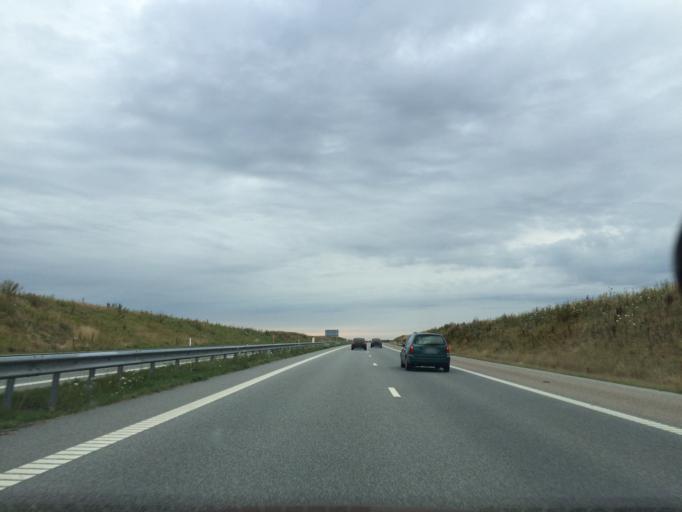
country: DK
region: South Denmark
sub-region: Sonderborg Kommune
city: Broager
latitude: 54.9386
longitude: 9.6711
